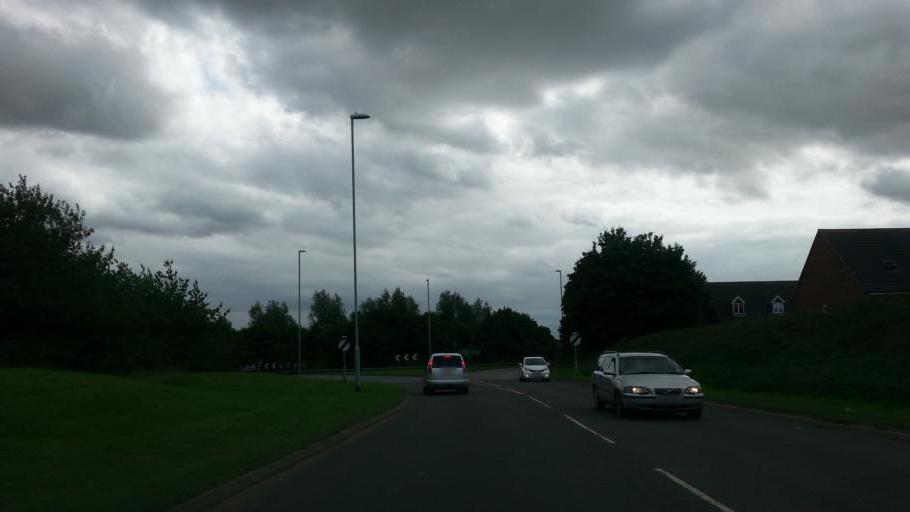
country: GB
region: England
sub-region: Northamptonshire
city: Earls Barton
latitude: 52.2527
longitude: -0.8091
